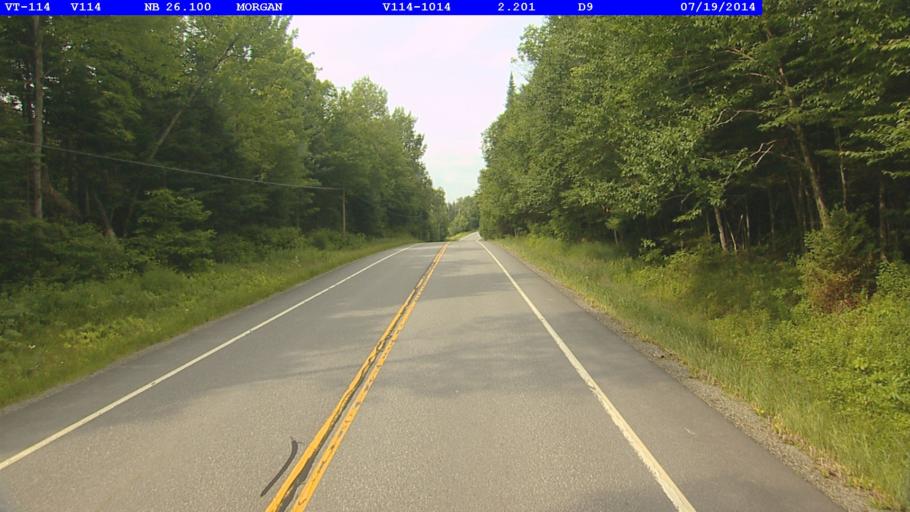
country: CA
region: Quebec
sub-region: Estrie
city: Coaticook
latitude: 44.8759
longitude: -71.8999
